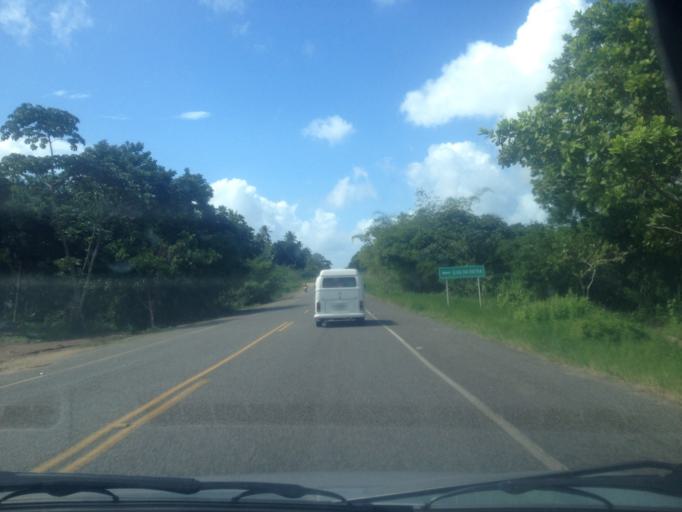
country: BR
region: Bahia
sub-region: Conde
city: Conde
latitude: -11.7737
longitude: -37.5989
